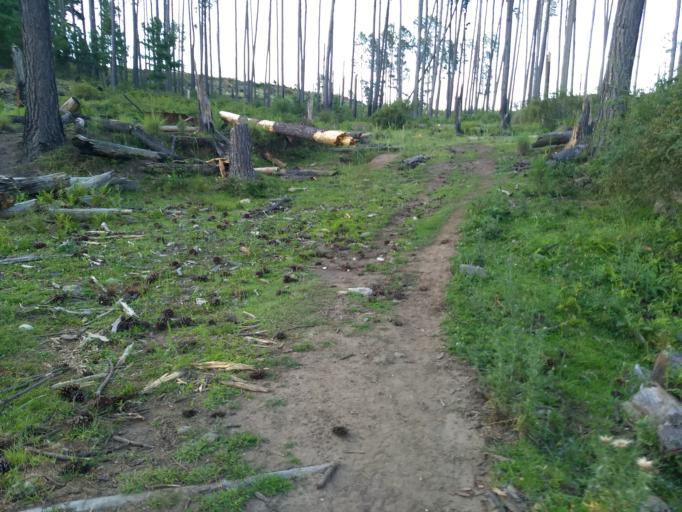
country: AR
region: Cordoba
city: Villa Berna
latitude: -31.9907
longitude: -64.8063
